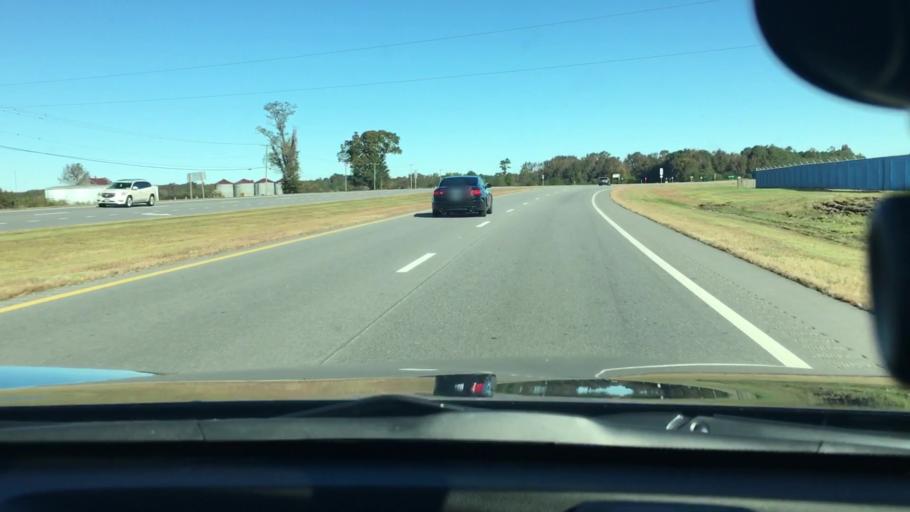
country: US
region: North Carolina
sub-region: Pitt County
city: Bethel
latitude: 35.7868
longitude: -77.3714
